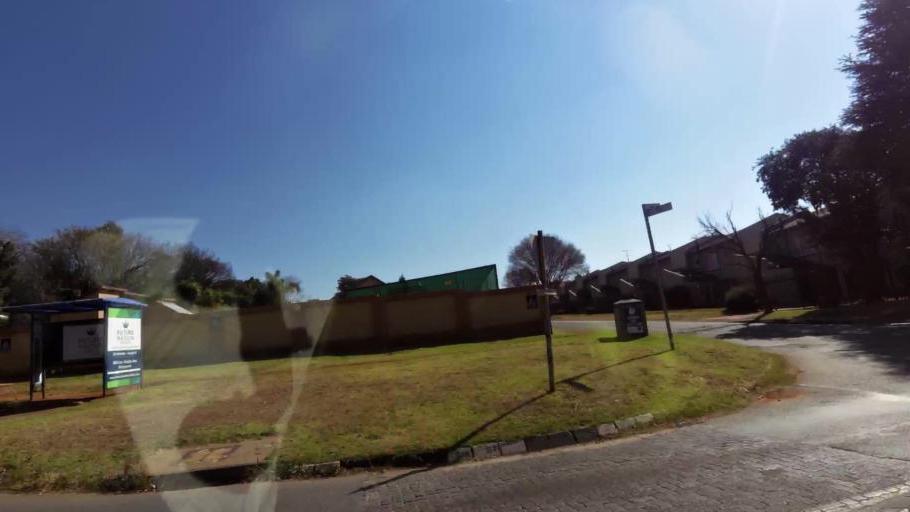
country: ZA
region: Gauteng
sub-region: City of Johannesburg Metropolitan Municipality
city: Roodepoort
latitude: -26.1355
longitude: 27.9415
